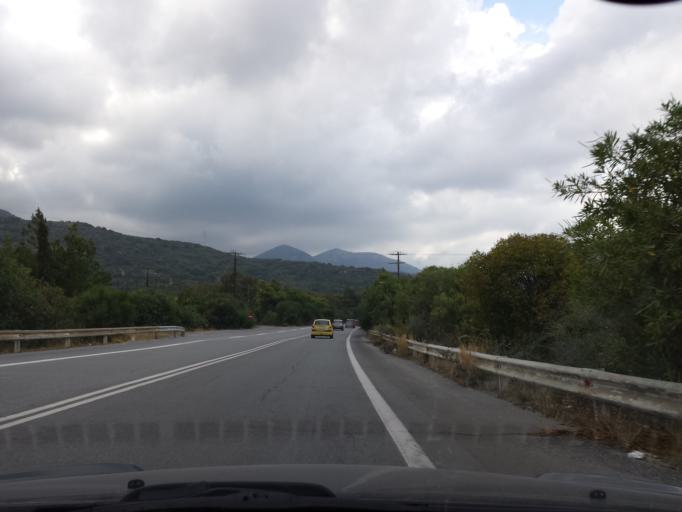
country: GR
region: Crete
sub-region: Nomos Lasithiou
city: Neapoli
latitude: 35.2609
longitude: 25.5984
